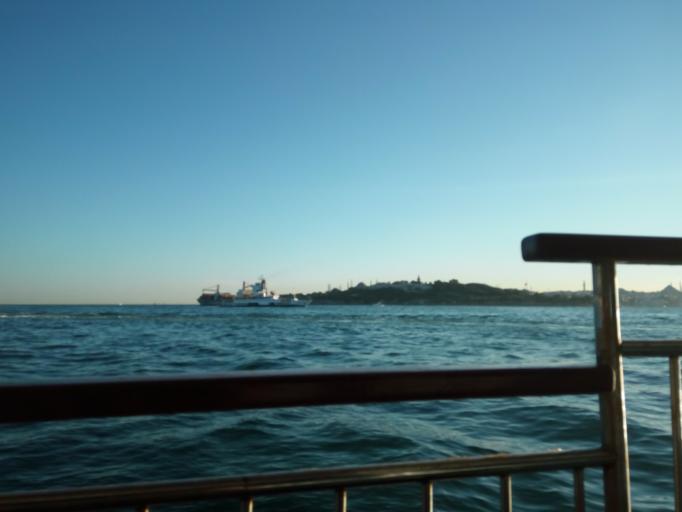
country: TR
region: Istanbul
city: UEskuedar
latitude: 41.0202
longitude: 29.0003
